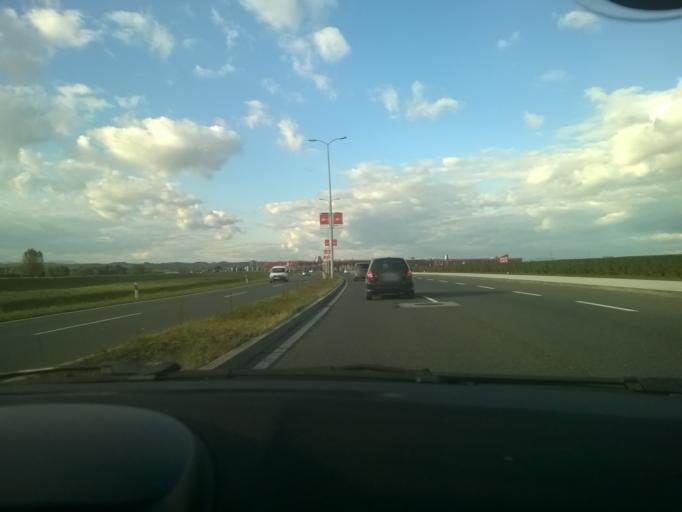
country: HR
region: Zagrebacka
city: Zapresic
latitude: 45.8644
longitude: 15.8274
